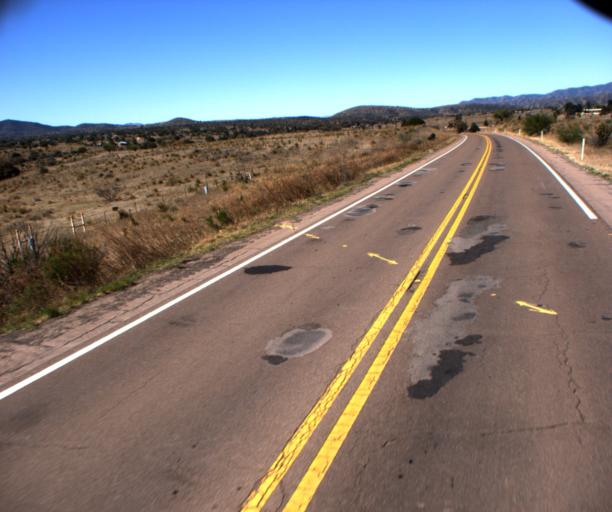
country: US
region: Arizona
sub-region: Pima County
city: Corona de Tucson
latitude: 31.6764
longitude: -110.6662
